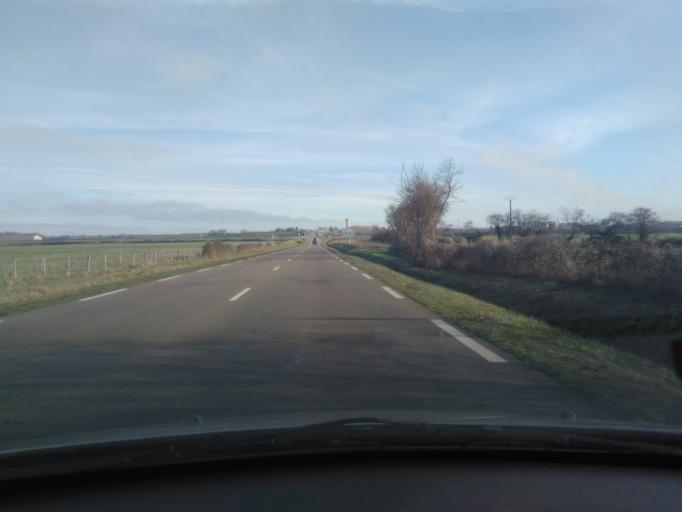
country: FR
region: Bourgogne
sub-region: Departement de la Nievre
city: Saint-Pierre-le-Moutier
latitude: 46.8018
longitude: 3.1031
